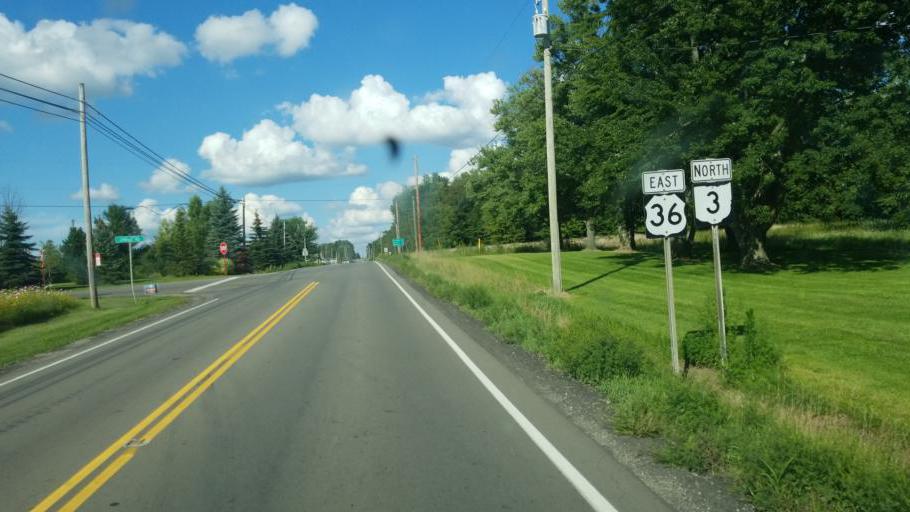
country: US
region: Ohio
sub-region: Knox County
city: Centerburg
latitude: 40.3187
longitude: -82.6752
